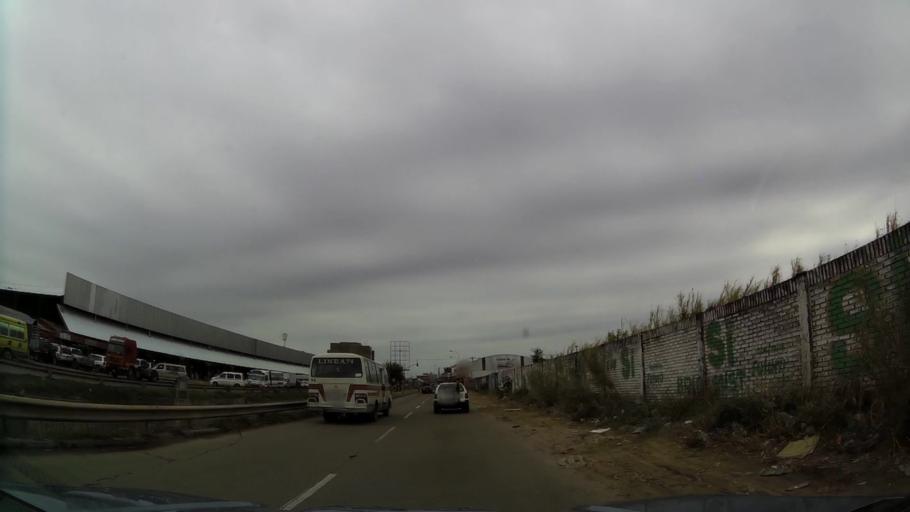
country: BO
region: Santa Cruz
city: Santa Cruz de la Sierra
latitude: -17.8226
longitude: -63.1638
